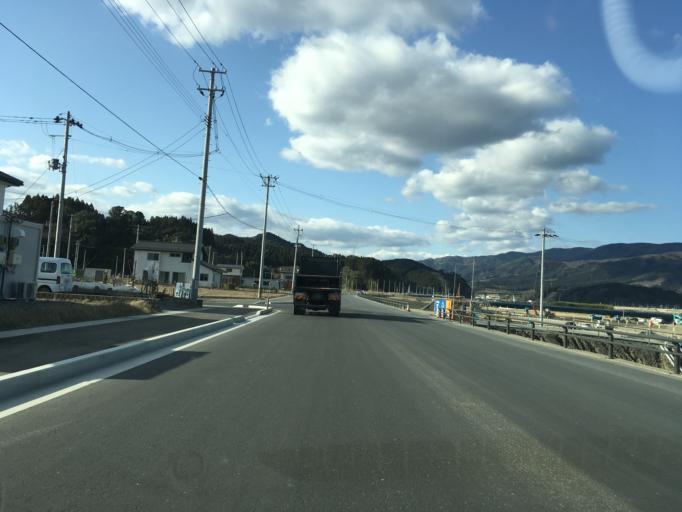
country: JP
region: Iwate
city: Ofunato
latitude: 39.0053
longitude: 141.6175
